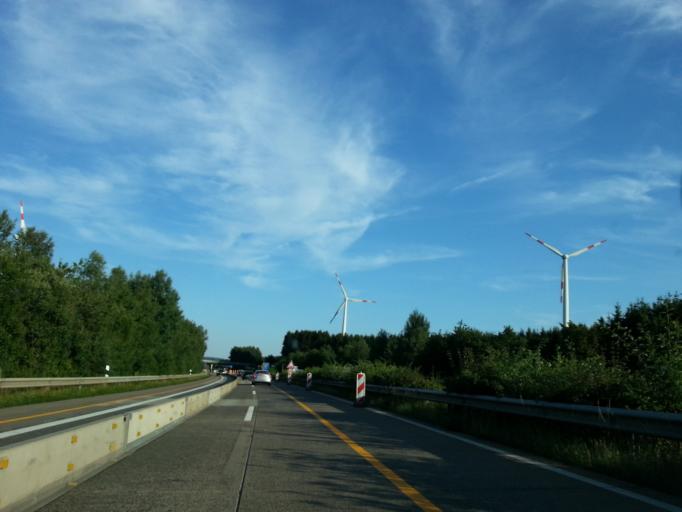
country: DE
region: Rheinland-Pfalz
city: Hinzert-Polert
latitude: 49.6959
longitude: 6.8910
